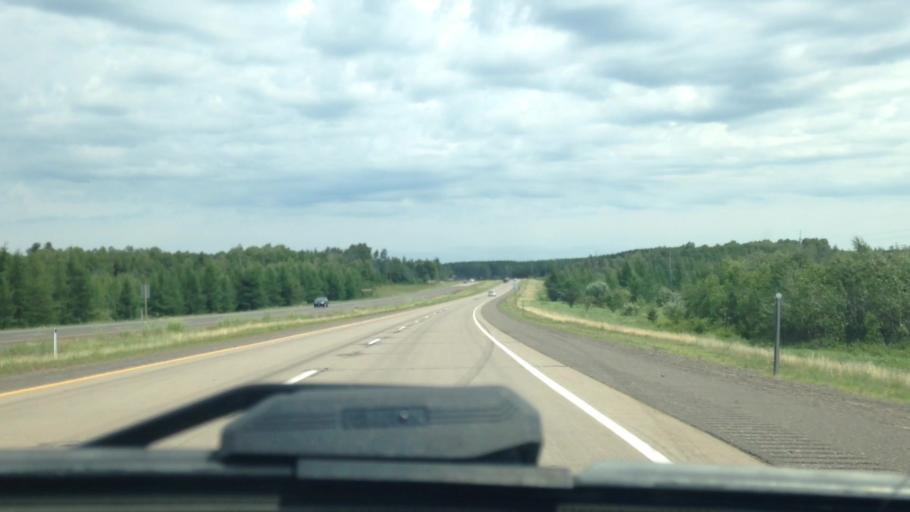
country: US
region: Wisconsin
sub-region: Douglas County
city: Lake Nebagamon
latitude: 46.1766
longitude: -91.8031
